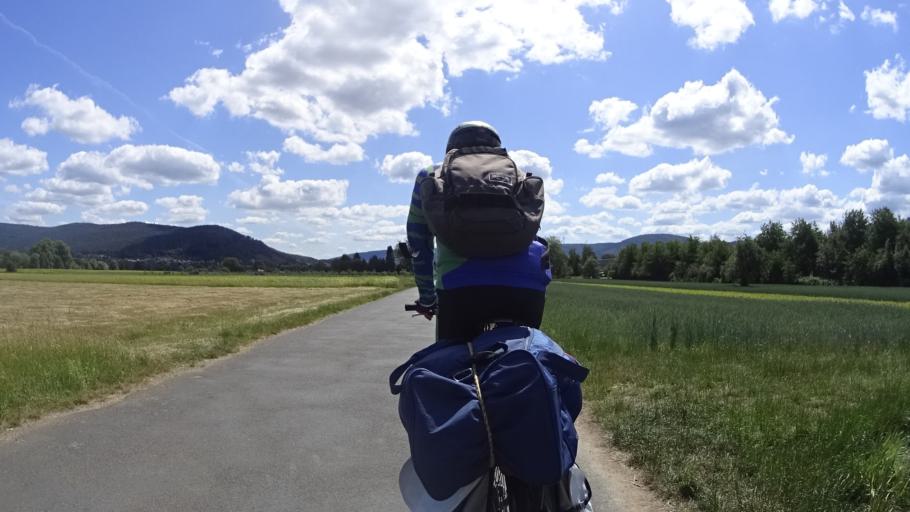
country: DE
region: Bavaria
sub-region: Regierungsbezirk Unterfranken
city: Kleinheubach
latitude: 49.7274
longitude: 9.2012
